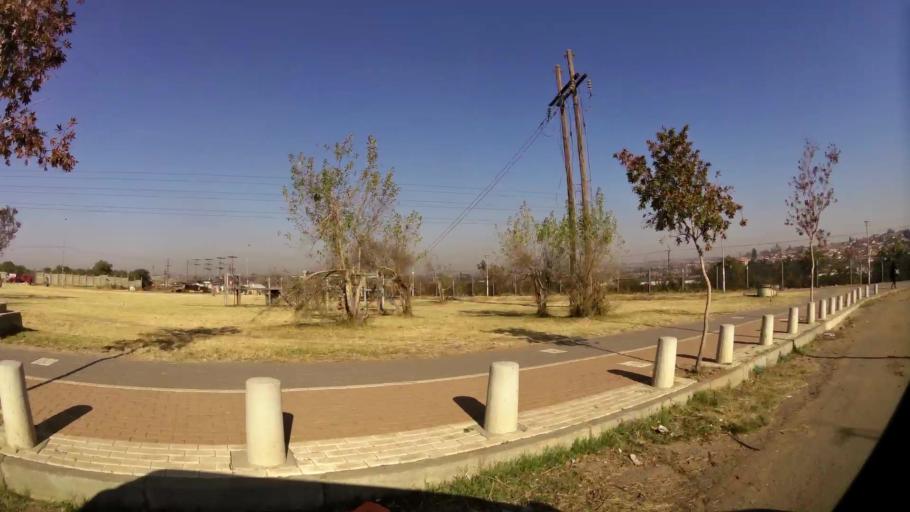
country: ZA
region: Gauteng
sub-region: City of Johannesburg Metropolitan Municipality
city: Soweto
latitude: -26.2444
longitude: 27.9134
